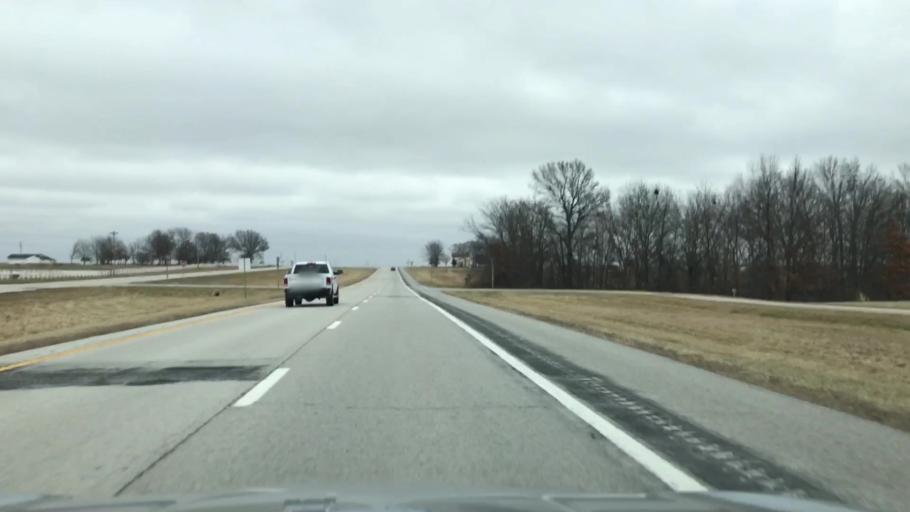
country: US
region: Missouri
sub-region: Linn County
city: Linneus
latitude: 39.7772
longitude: -93.3495
